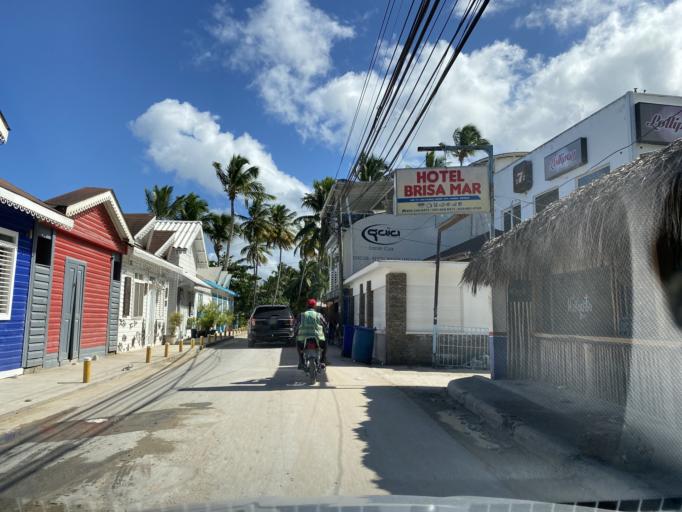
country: DO
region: Samana
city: Las Terrenas
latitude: 19.3224
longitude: -69.5415
